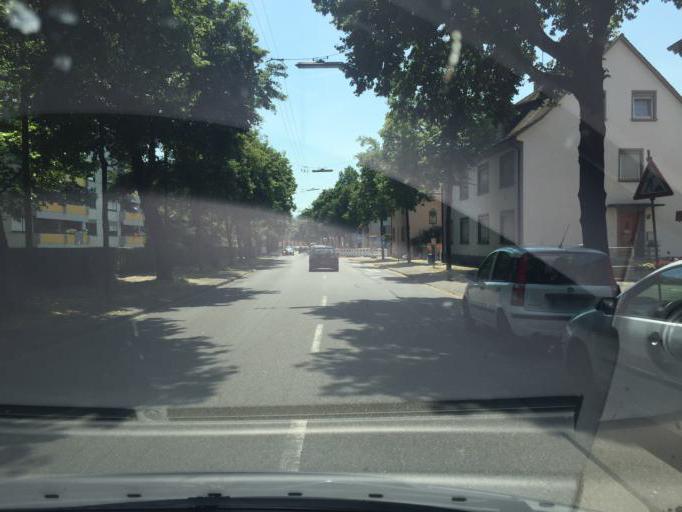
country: DE
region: Baden-Wuerttemberg
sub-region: Freiburg Region
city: Singen
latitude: 47.7482
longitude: 8.8430
